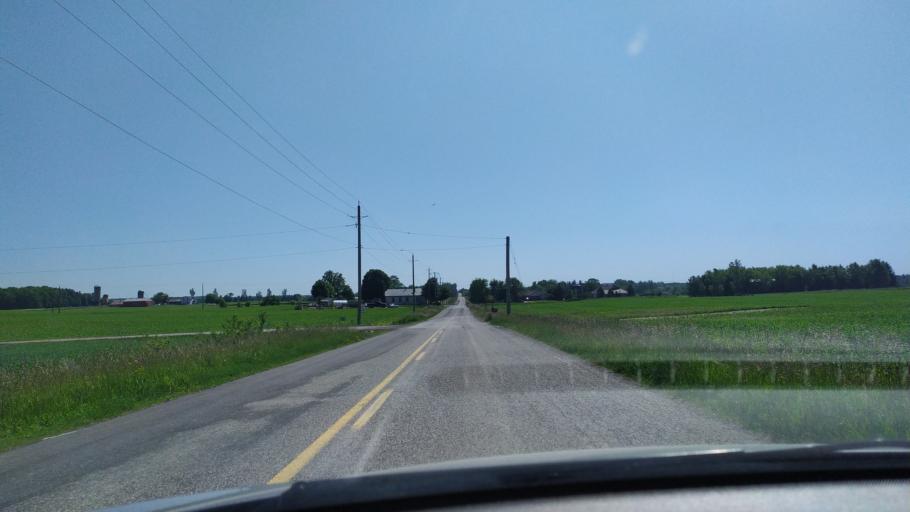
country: CA
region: Ontario
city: Waterloo
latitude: 43.4594
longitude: -80.7141
